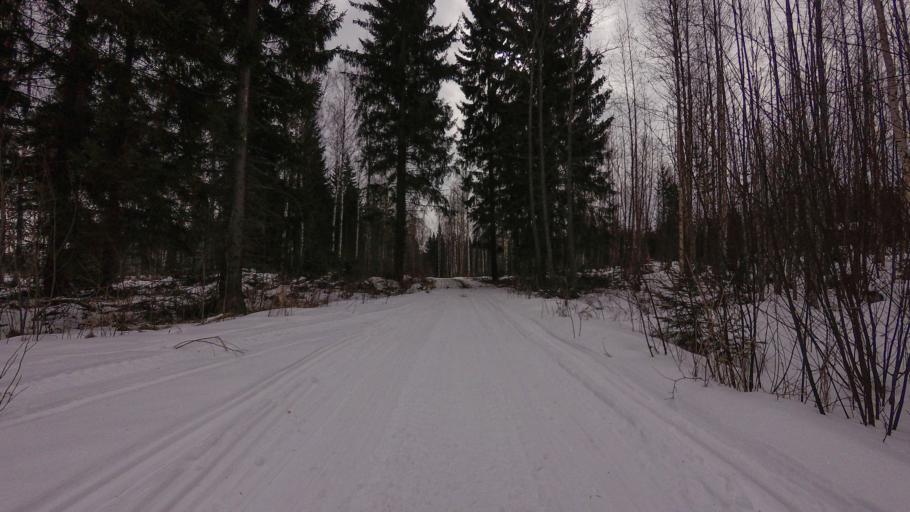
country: FI
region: Southern Savonia
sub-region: Savonlinna
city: Enonkoski
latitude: 62.1196
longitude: 28.6229
